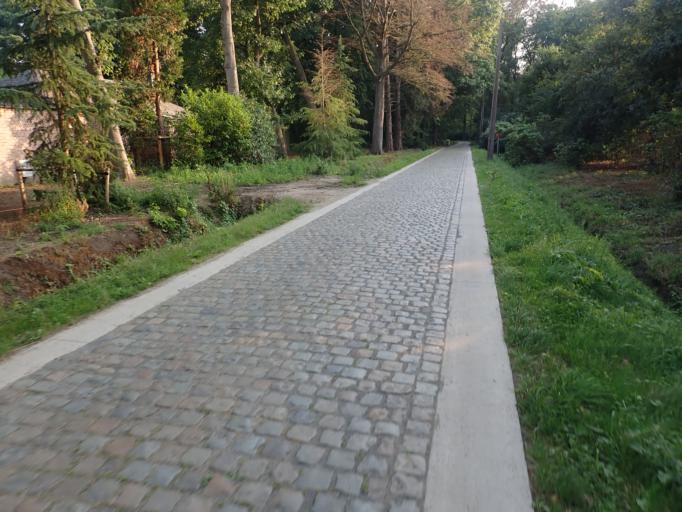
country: BE
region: Flanders
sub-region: Provincie Antwerpen
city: Berlaar
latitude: 51.1323
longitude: 4.6462
